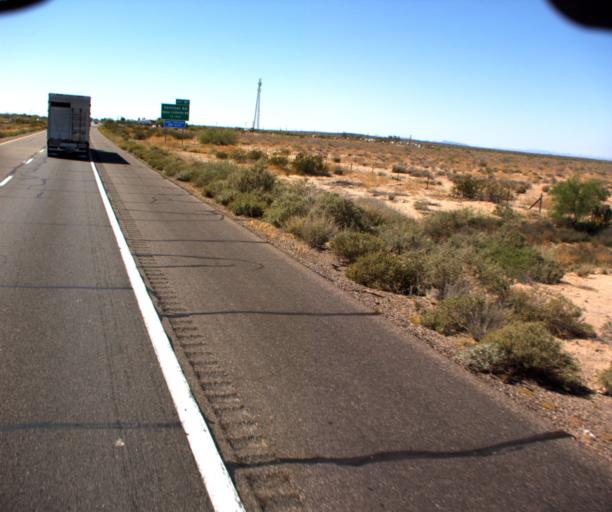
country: US
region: Arizona
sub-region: Maricopa County
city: Gila Bend
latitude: 32.8598
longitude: -113.1995
